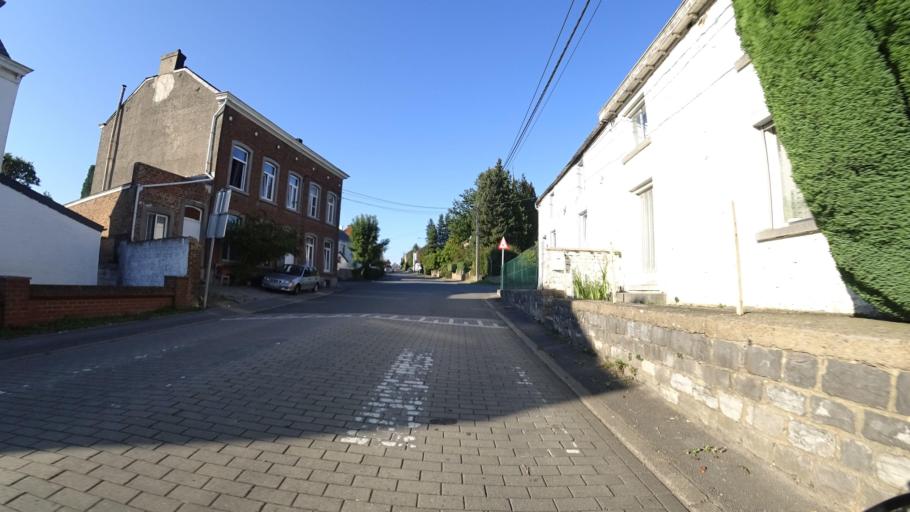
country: BE
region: Wallonia
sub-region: Province de Namur
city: Namur
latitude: 50.4913
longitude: 4.8473
